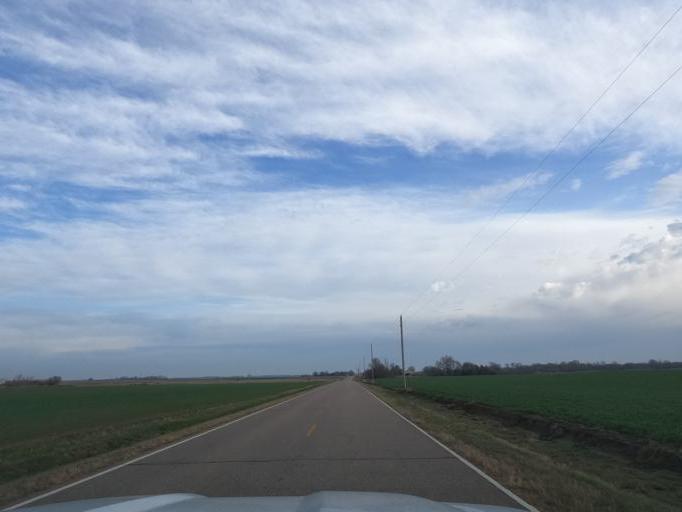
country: US
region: Kansas
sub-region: Reno County
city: Nickerson
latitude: 38.0402
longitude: -98.1790
